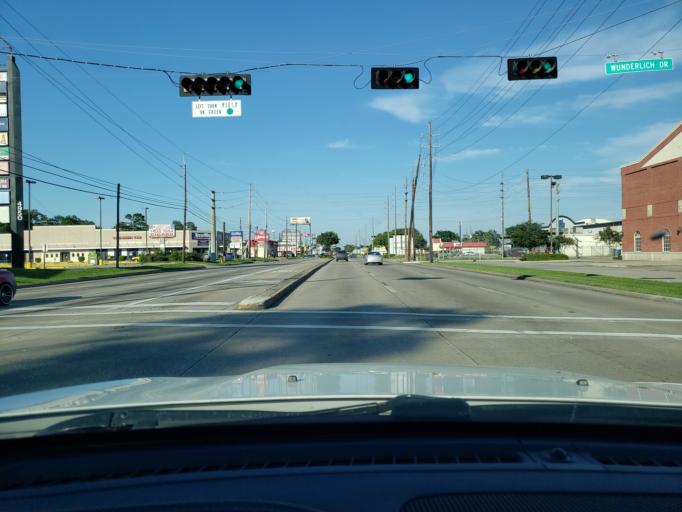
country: US
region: Texas
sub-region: Harris County
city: Hudson
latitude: 29.9841
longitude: -95.5053
